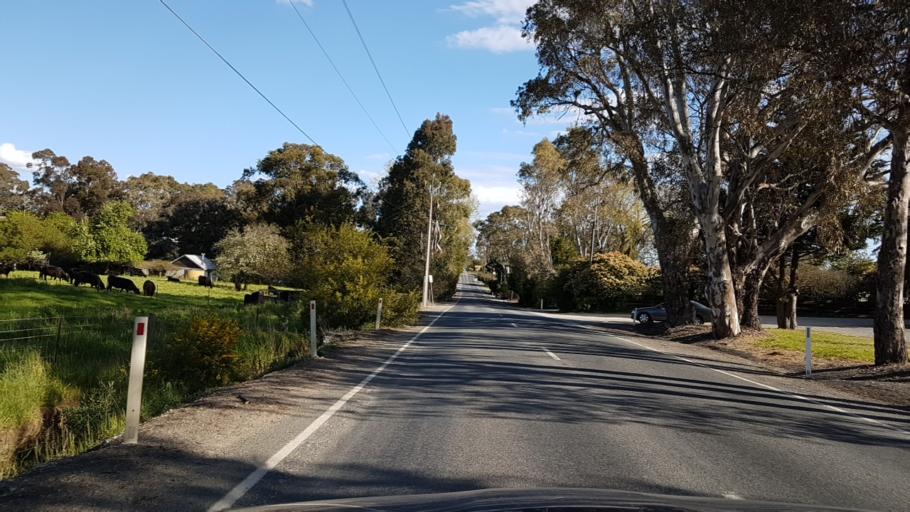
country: AU
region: South Australia
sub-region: Adelaide Hills
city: Lobethal
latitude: -34.8927
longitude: 138.8794
